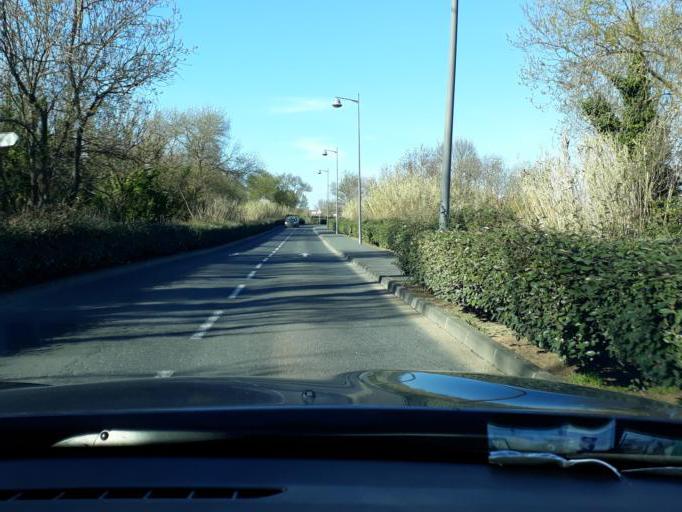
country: FR
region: Languedoc-Roussillon
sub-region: Departement de l'Herault
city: Agde
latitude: 43.3128
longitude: 3.4641
